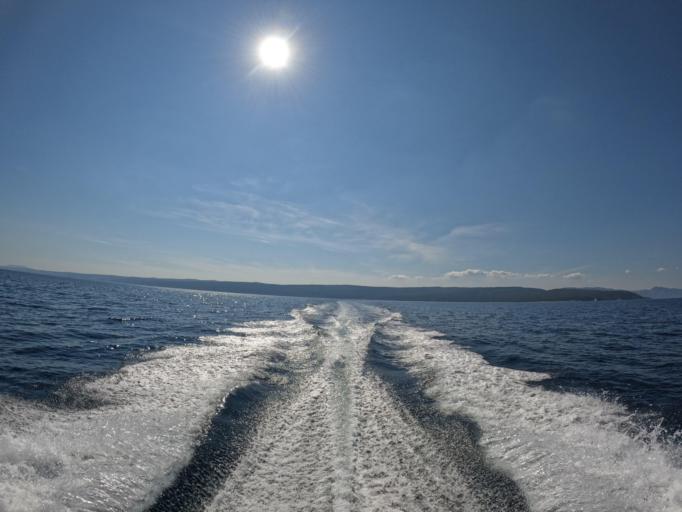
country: HR
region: Primorsko-Goranska
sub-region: Grad Krk
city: Krk
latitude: 44.9462
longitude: 14.5200
